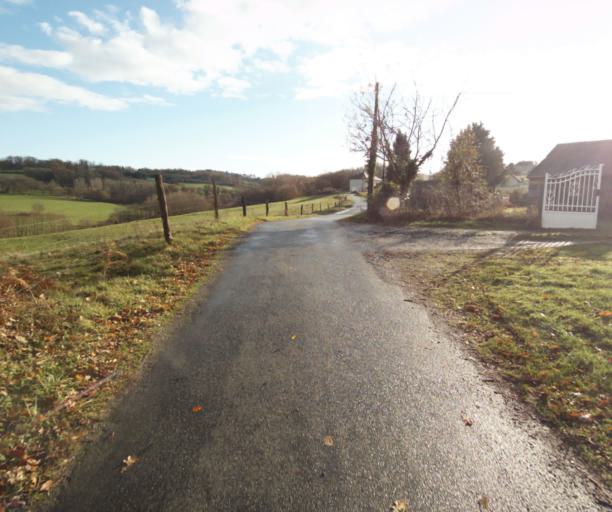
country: FR
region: Limousin
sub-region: Departement de la Correze
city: Sainte-Fereole
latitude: 45.2497
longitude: 1.6070
